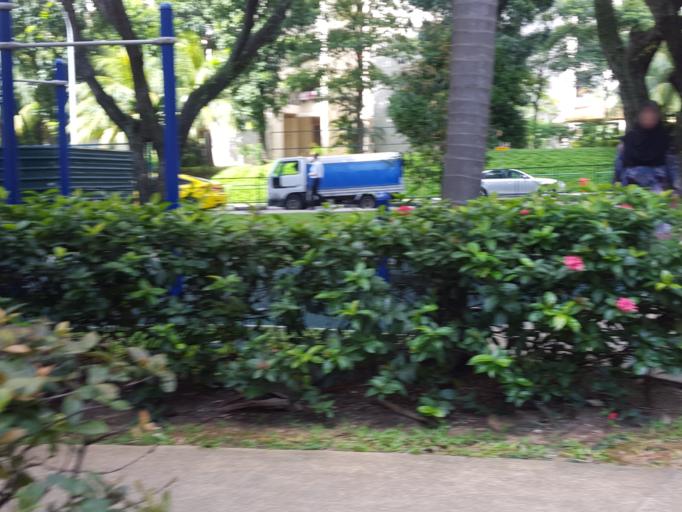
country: SG
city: Singapore
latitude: 1.3350
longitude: 103.8472
